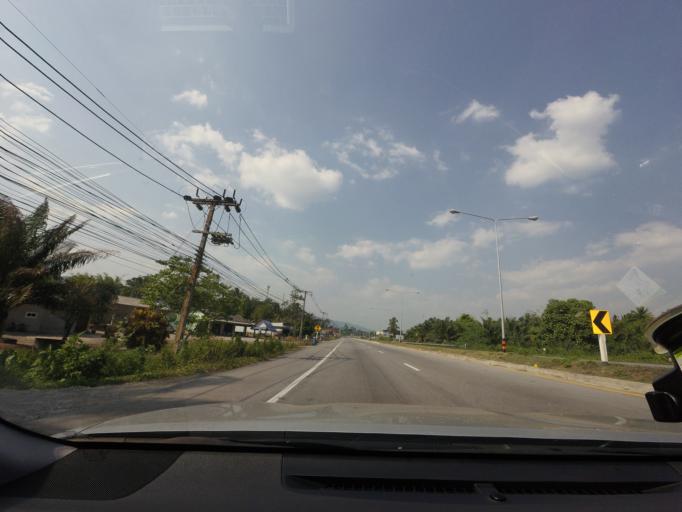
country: TH
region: Phangnga
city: Thap Put
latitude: 8.5738
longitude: 98.7406
